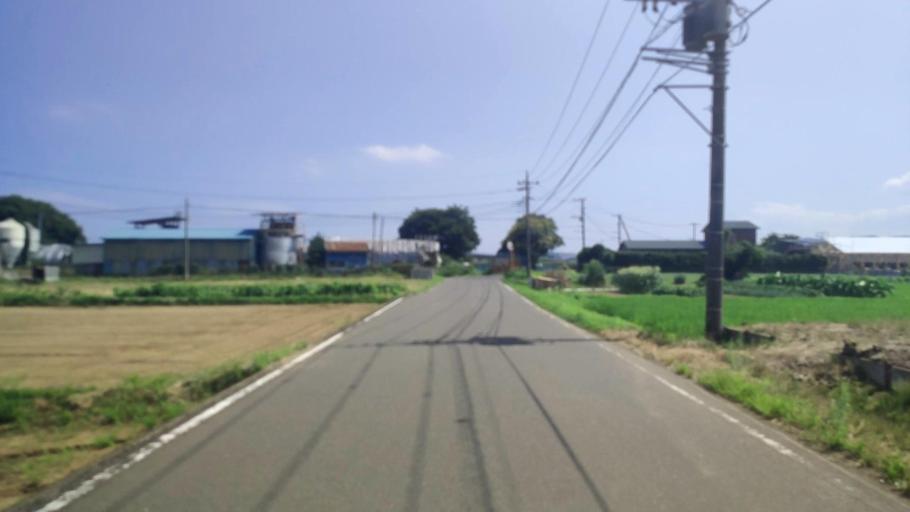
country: JP
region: Kanagawa
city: Isehara
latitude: 35.3684
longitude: 139.3072
